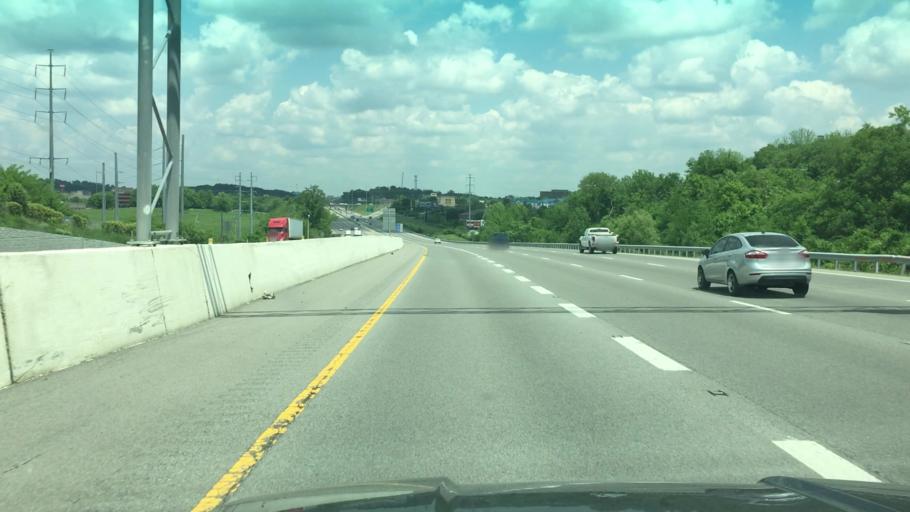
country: US
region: Tennessee
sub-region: Williamson County
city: Franklin
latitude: 35.9036
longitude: -86.8261
